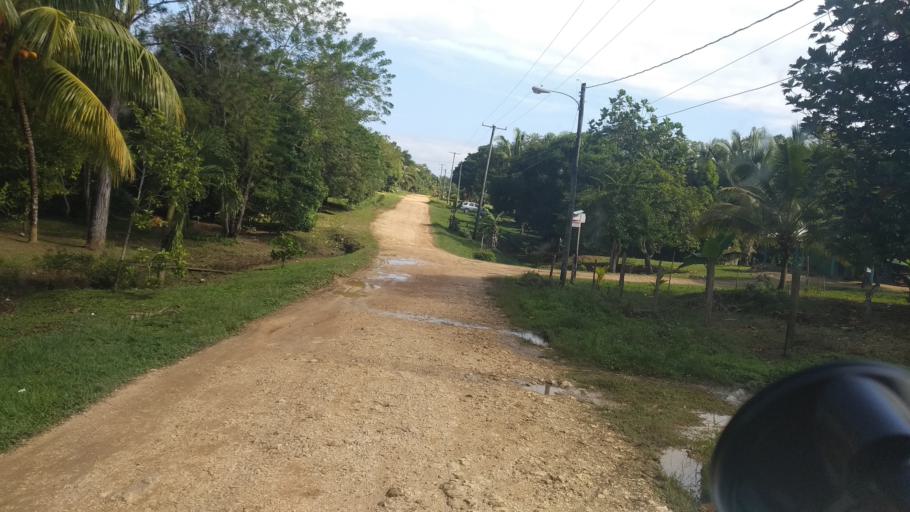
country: BZ
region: Toledo
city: Punta Gorda
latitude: 16.2120
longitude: -88.9111
